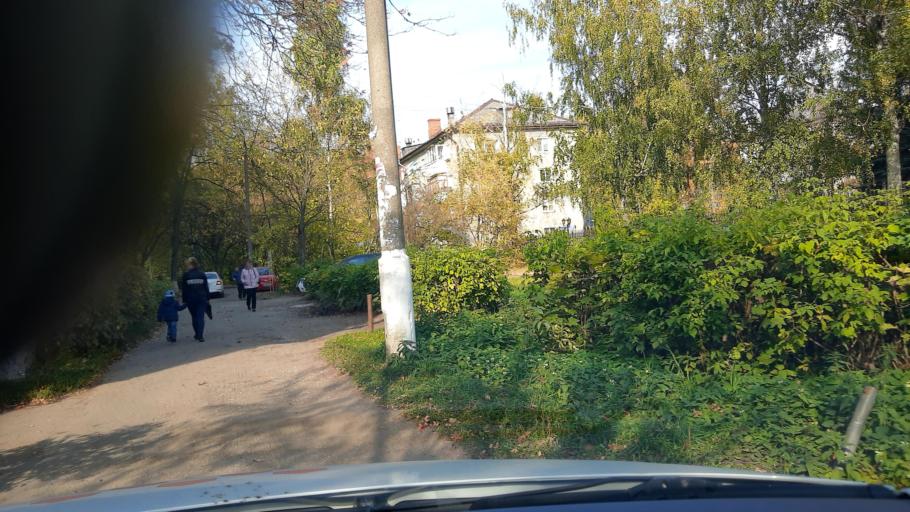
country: RU
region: Moskovskaya
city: Elektrostal'
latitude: 55.8009
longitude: 38.4394
